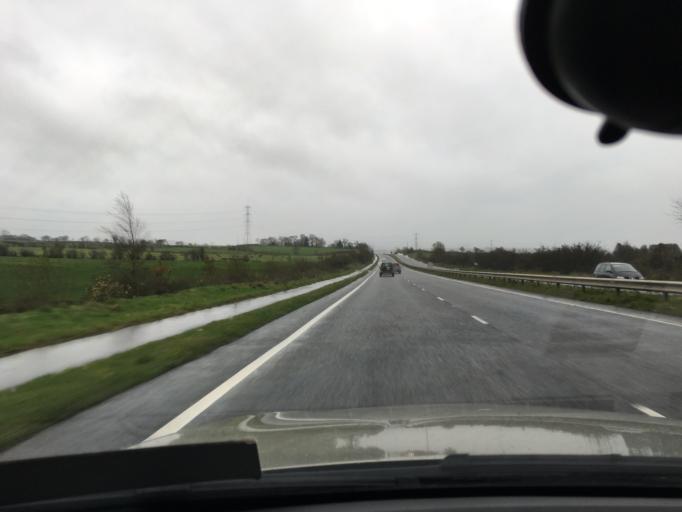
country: GB
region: Northern Ireland
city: Carnmoney
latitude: 54.7193
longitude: -5.9683
